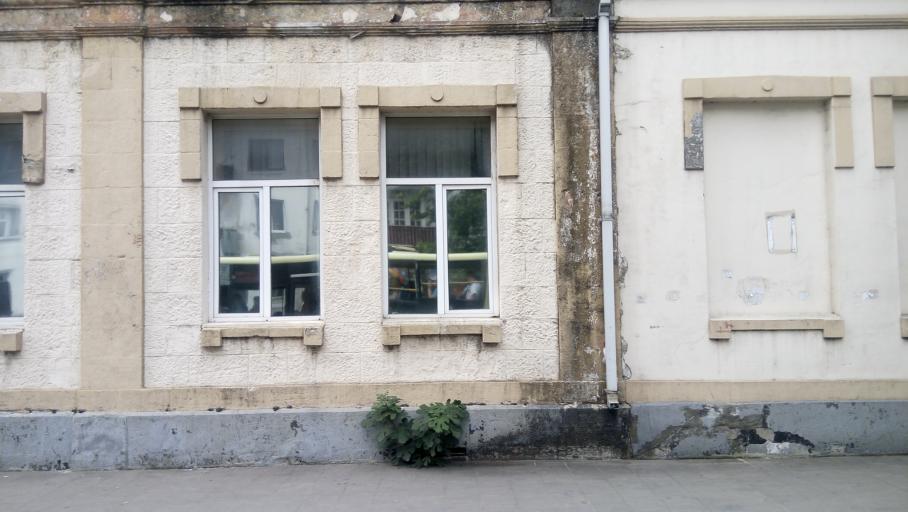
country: GE
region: Ajaria
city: Batumi
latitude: 41.6450
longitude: 41.6491
